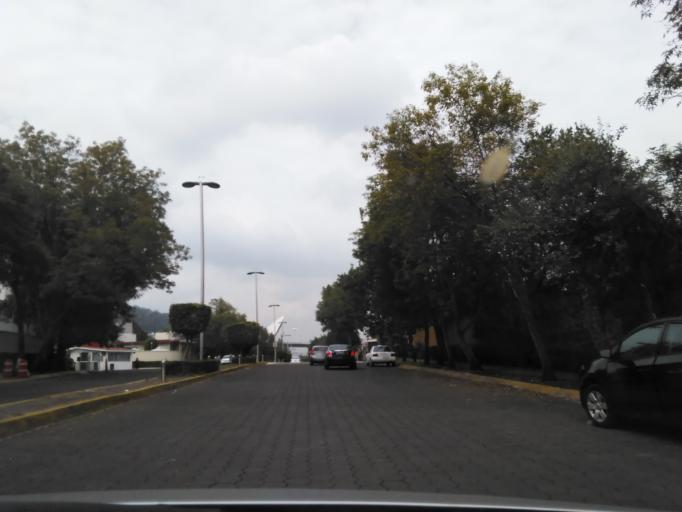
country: MX
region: Mexico City
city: Tlalpan
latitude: 19.2971
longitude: -99.1923
